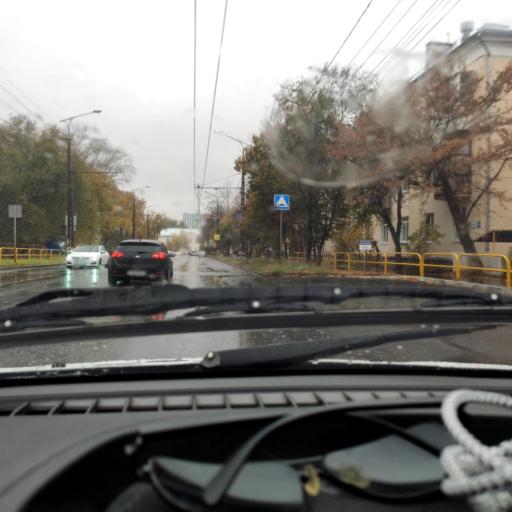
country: RU
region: Samara
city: Tol'yatti
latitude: 53.5216
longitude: 49.4235
